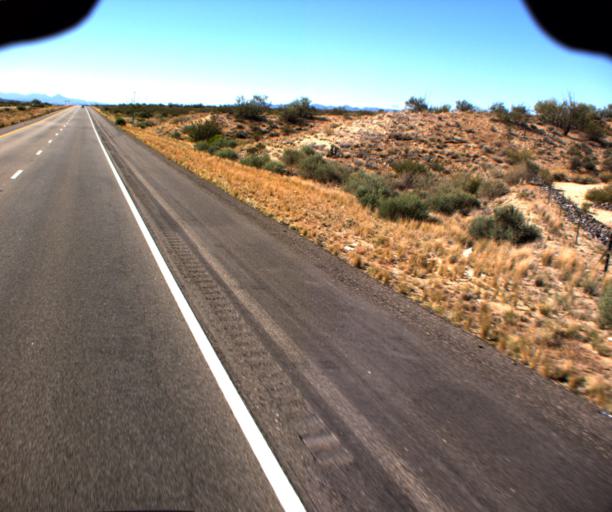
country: US
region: Arizona
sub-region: Mohave County
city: Kingman
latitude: 34.8577
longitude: -113.6405
